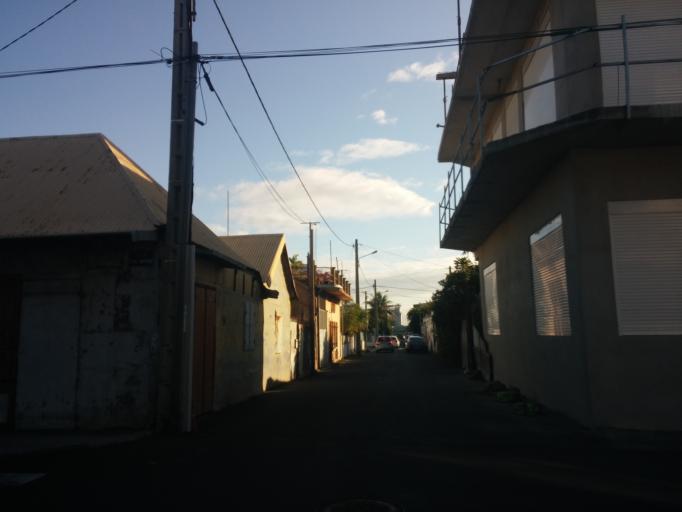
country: RE
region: Reunion
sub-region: Reunion
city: Le Port
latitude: -20.9353
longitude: 55.2928
